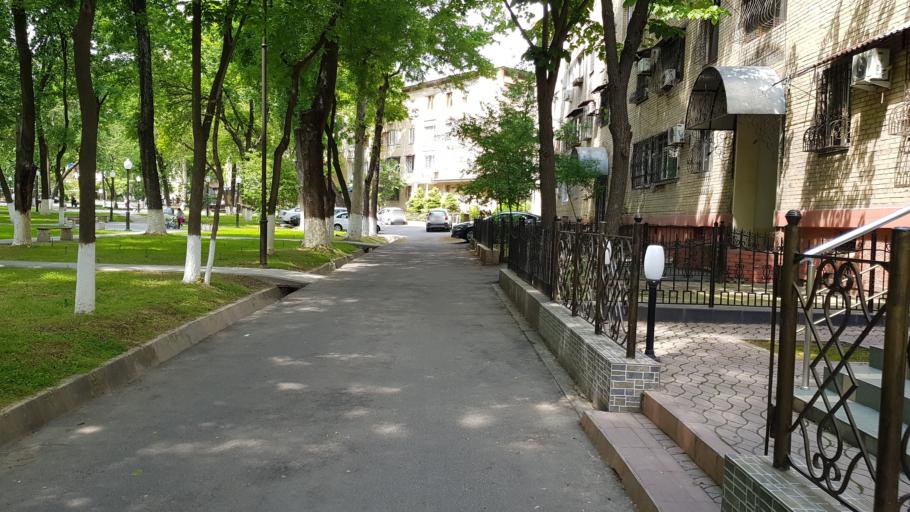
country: UZ
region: Toshkent Shahri
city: Tashkent
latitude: 41.3123
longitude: 69.2926
